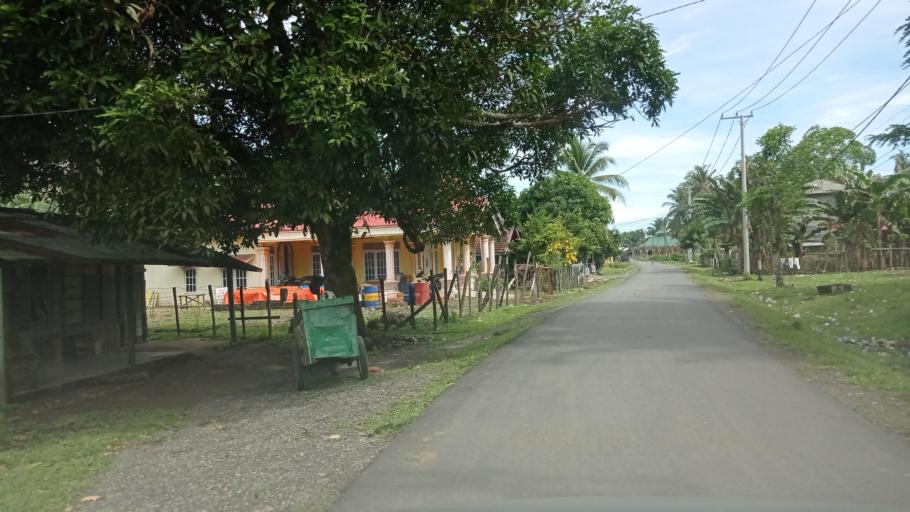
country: ID
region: Bengkulu
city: Ipuh
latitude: -2.5885
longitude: 101.1167
